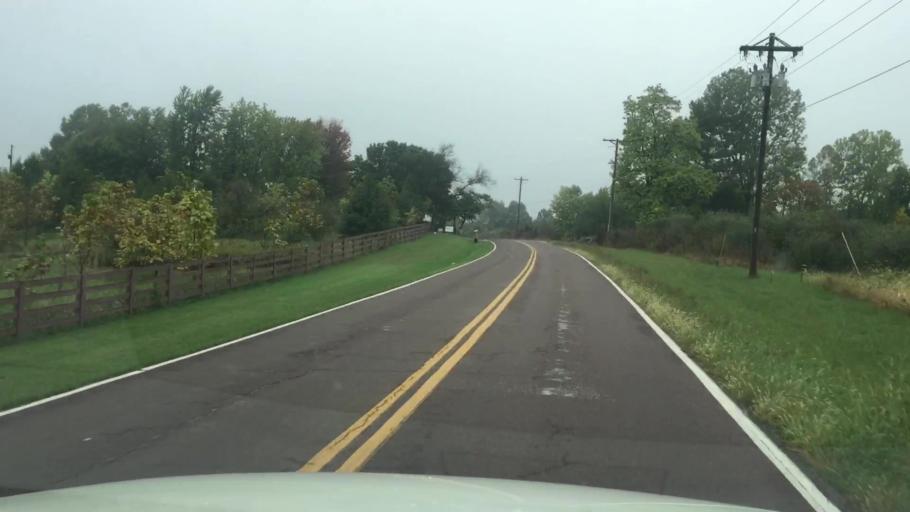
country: US
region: Missouri
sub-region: Boone County
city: Columbia
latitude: 38.8591
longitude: -92.3217
